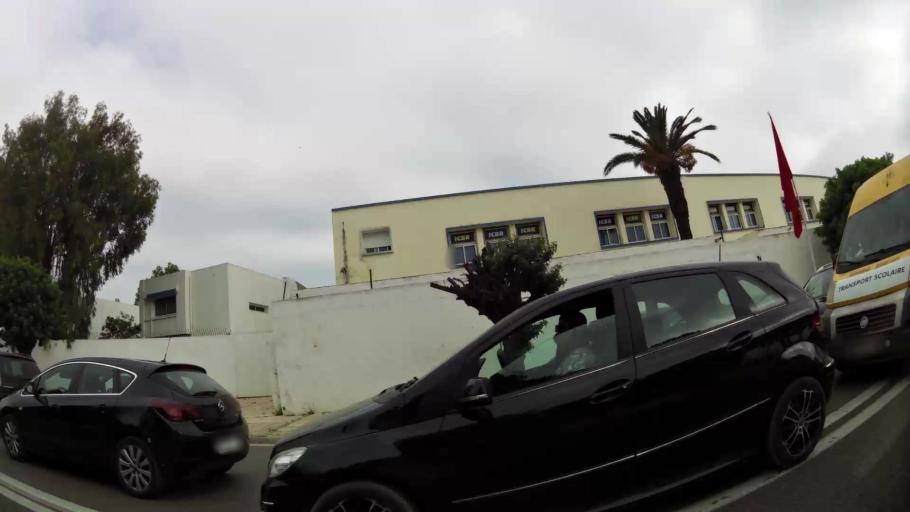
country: MA
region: Rabat-Sale-Zemmour-Zaer
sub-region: Rabat
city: Rabat
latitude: 34.0189
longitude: -6.8209
